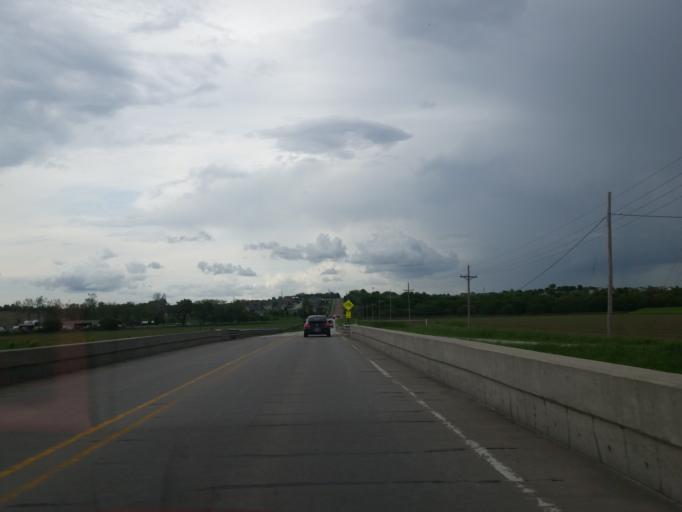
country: US
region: Nebraska
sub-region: Sarpy County
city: Offutt Air Force Base
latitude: 41.1414
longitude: -95.9475
